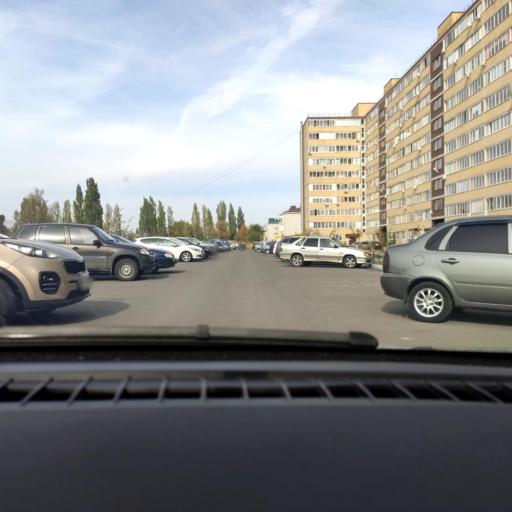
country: RU
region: Voronezj
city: Novaya Usman'
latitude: 51.6077
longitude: 39.3791
